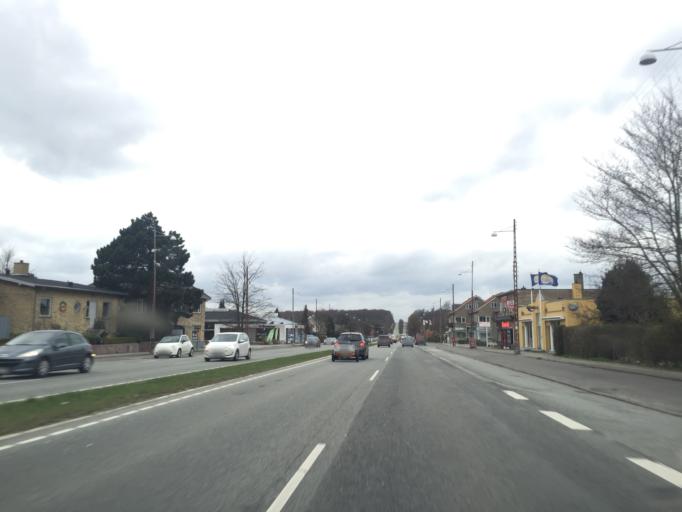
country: DK
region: Capital Region
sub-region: Rudersdal Kommune
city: Holte
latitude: 55.7933
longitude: 12.4845
